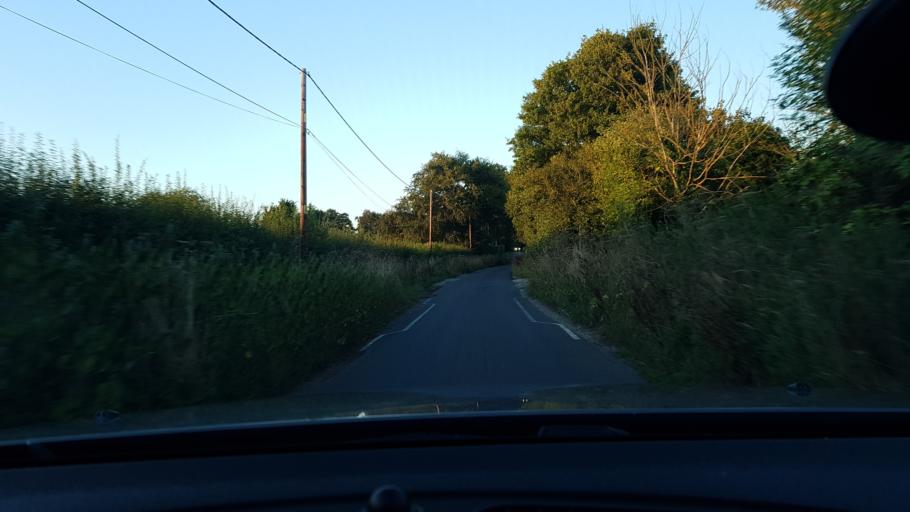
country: GB
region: England
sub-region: West Berkshire
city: Hungerford
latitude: 51.3958
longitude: -1.5209
